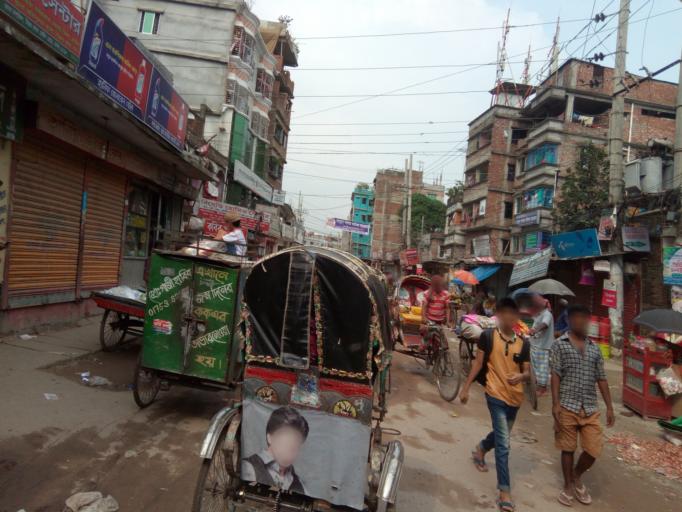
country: BD
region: Dhaka
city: Paltan
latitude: 23.7299
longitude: 90.4388
